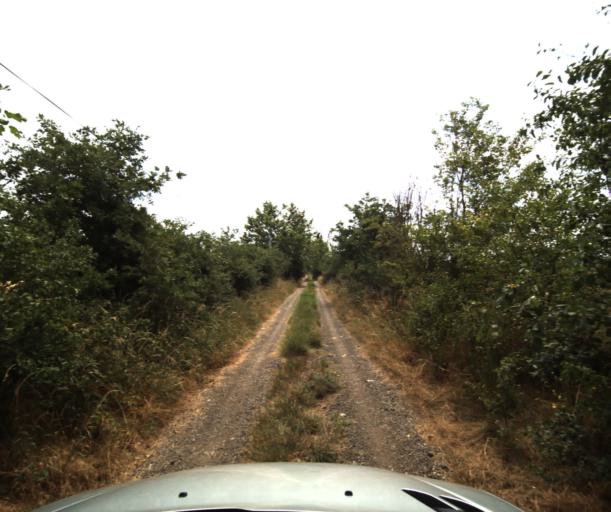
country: FR
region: Midi-Pyrenees
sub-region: Departement de la Haute-Garonne
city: Lacasse
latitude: 43.4127
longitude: 1.2658
